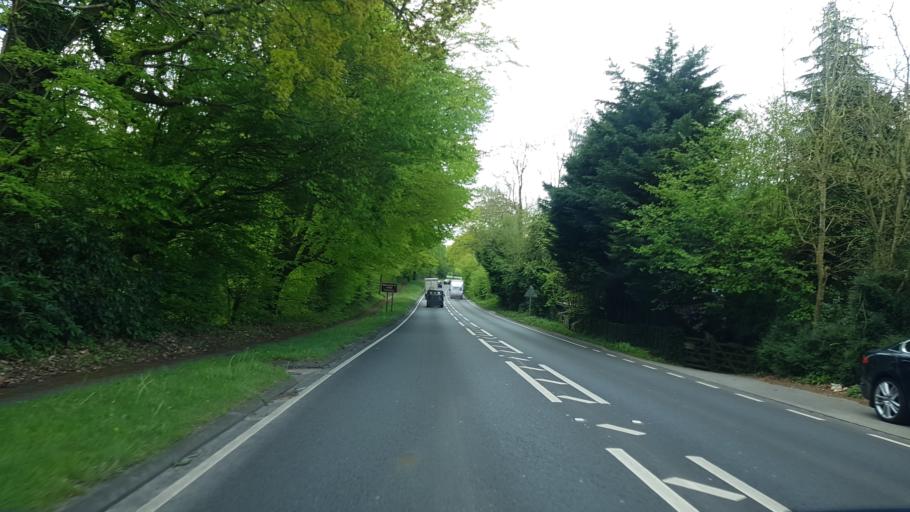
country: GB
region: England
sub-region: Kent
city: Hawkhurst
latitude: 51.0490
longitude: 0.4484
